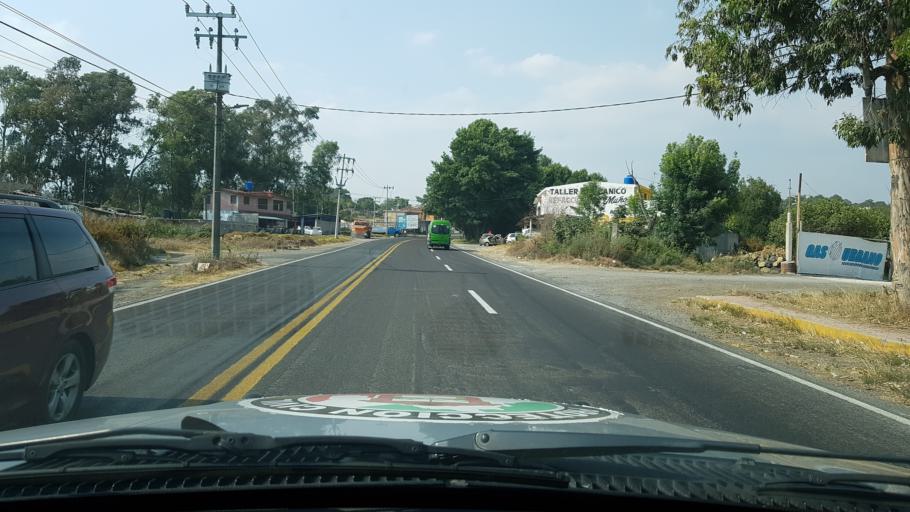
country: MX
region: Mexico
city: Tepetlixpa
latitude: 19.0197
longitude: -98.8246
